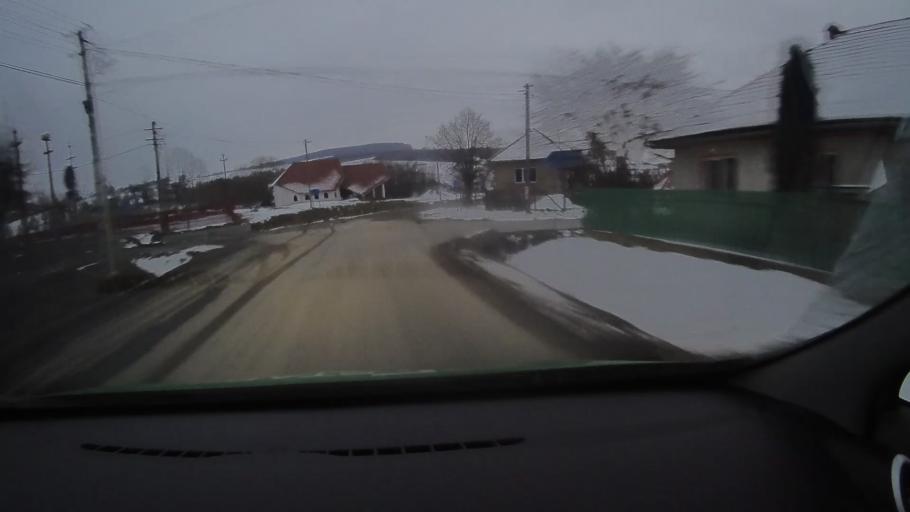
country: RO
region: Harghita
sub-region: Comuna Darjiu
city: Darjiu
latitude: 46.2101
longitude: 25.2414
